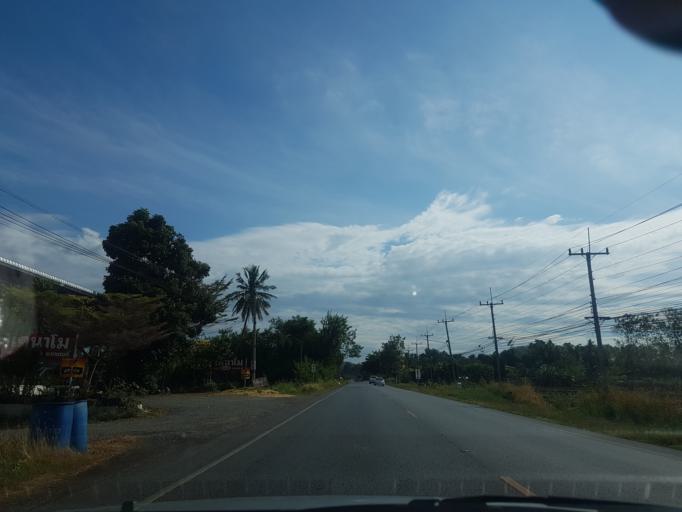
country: TH
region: Sara Buri
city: Phra Phutthabat
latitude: 14.8023
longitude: 100.7468
